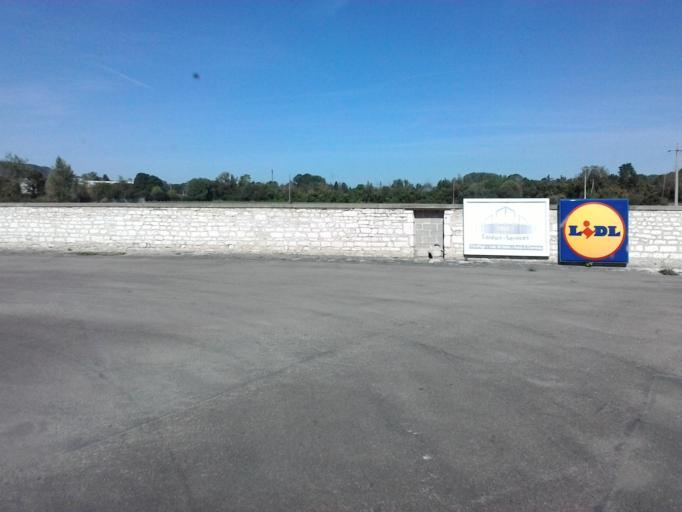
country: FR
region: Bourgogne
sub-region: Departement de l'Yonne
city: Tonnerre
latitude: 47.8537
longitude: 3.9852
